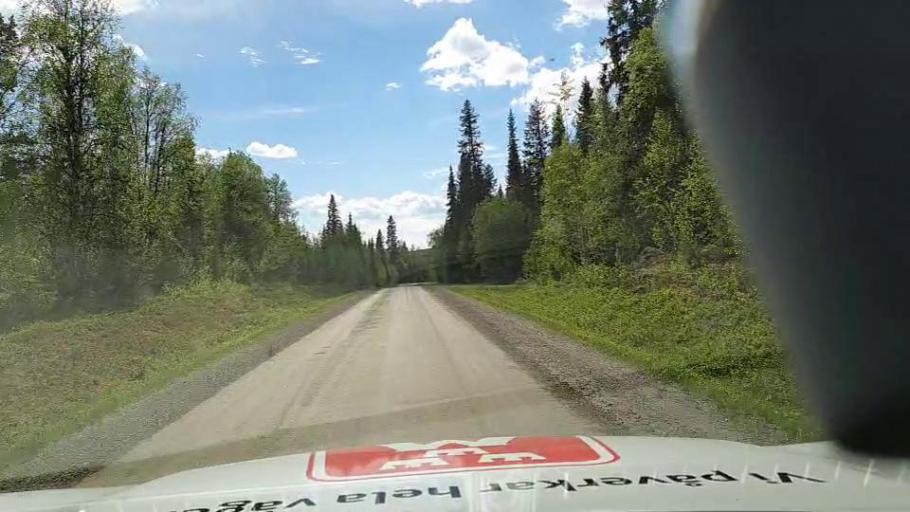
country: SE
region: Vaesterbotten
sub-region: Vilhelmina Kommun
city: Sjoberg
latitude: 64.5527
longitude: 15.8060
